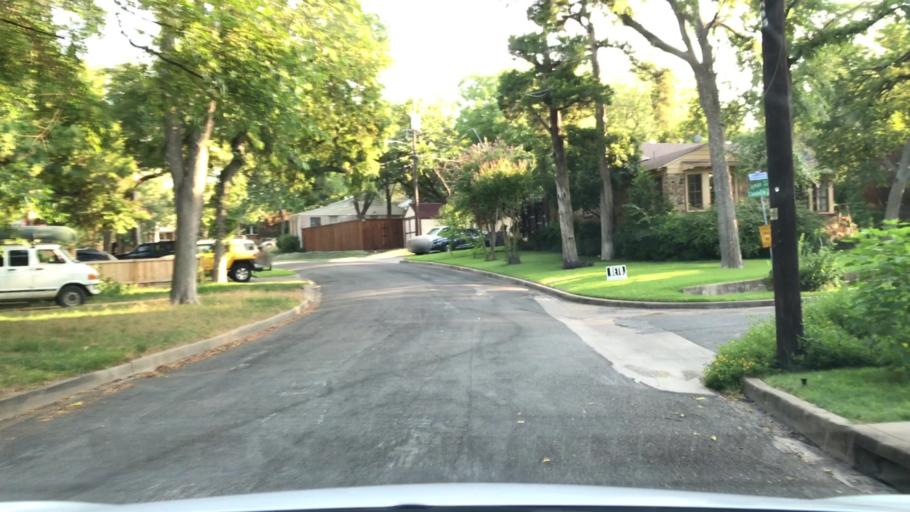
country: US
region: Texas
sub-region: Dallas County
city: Cockrell Hill
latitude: 32.7433
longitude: -96.8666
